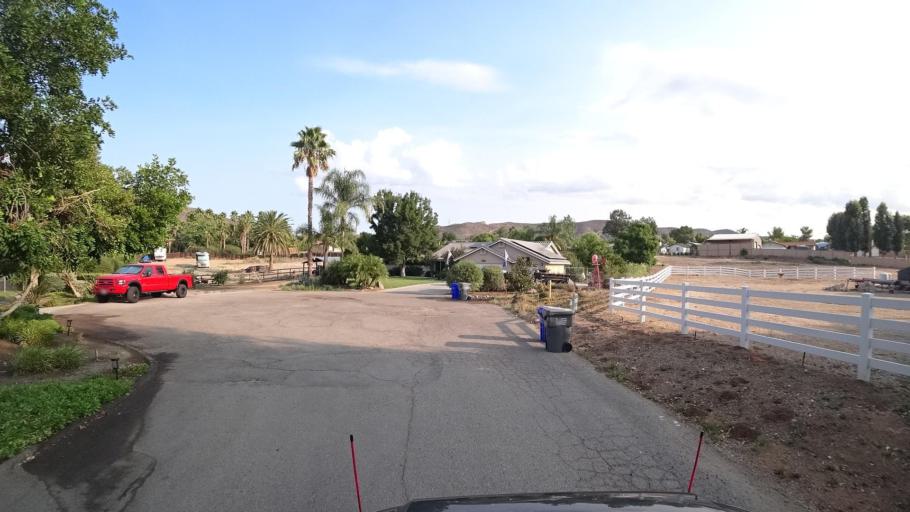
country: US
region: California
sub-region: San Diego County
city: San Diego Country Estates
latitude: 33.0139
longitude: -116.8156
